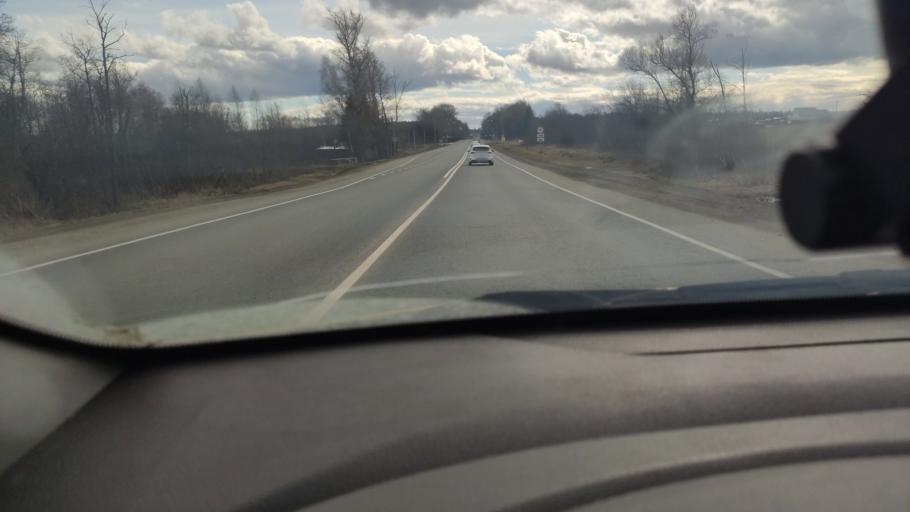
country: RU
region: Moskovskaya
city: Dorokhovo
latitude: 55.5940
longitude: 36.3635
